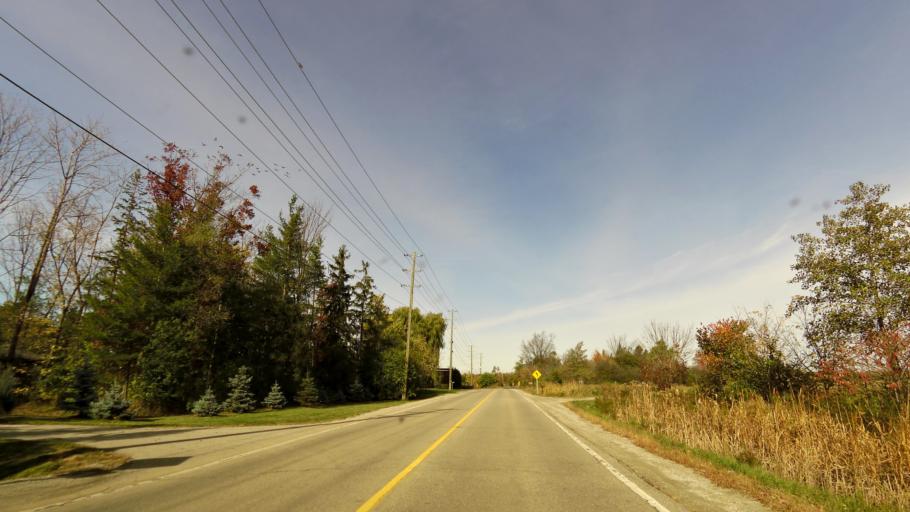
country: CA
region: Ontario
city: Oakville
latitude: 43.5115
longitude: -79.7717
